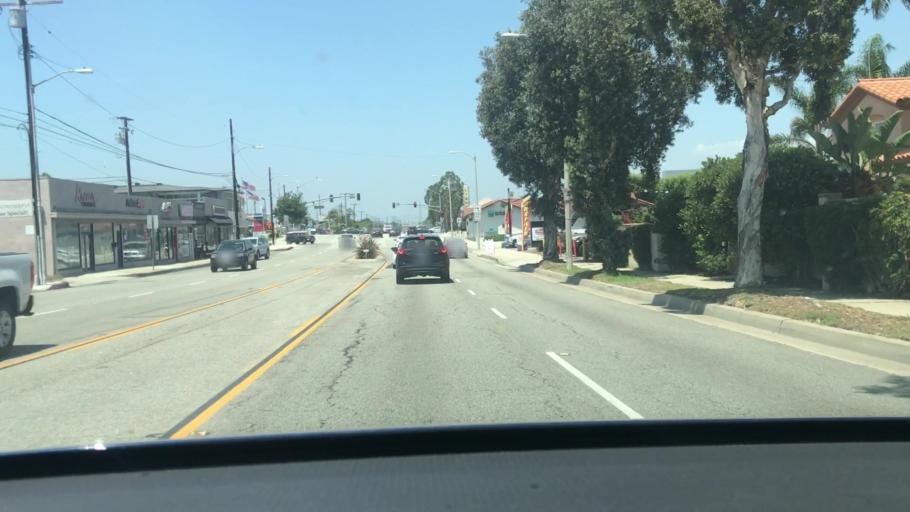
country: US
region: California
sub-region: Los Angeles County
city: Lawndale
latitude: 33.8858
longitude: -118.3786
